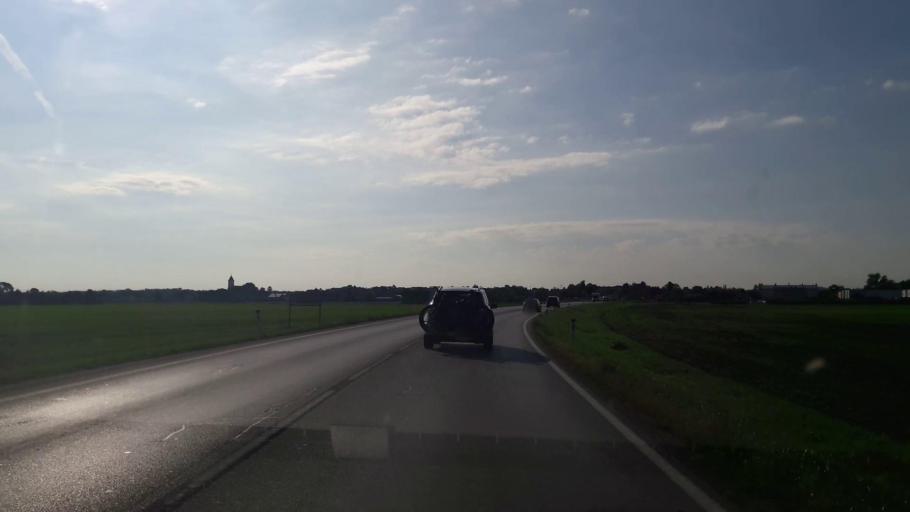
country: AT
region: Burgenland
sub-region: Eisenstadt-Umgebung
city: Trausdorf an der Wulka
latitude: 47.8187
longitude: 16.5439
